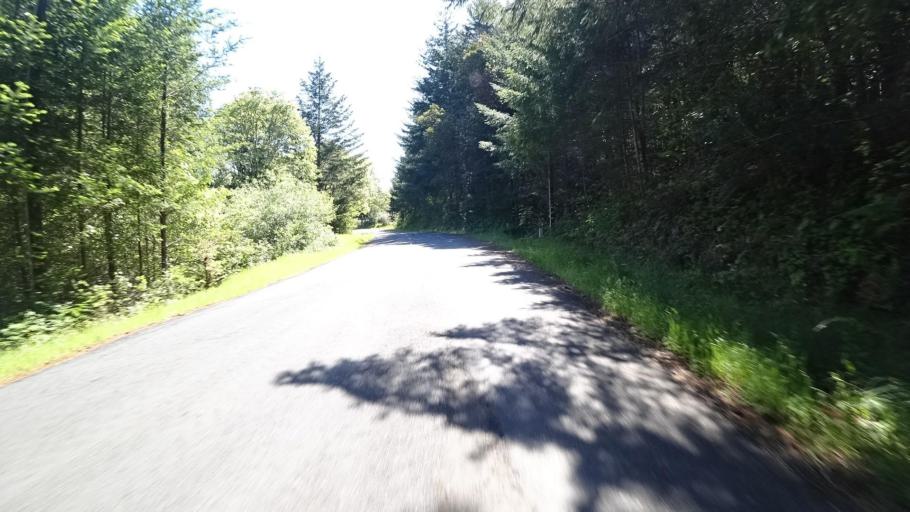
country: US
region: California
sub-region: Humboldt County
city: Rio Dell
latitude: 40.2491
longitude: -124.1755
